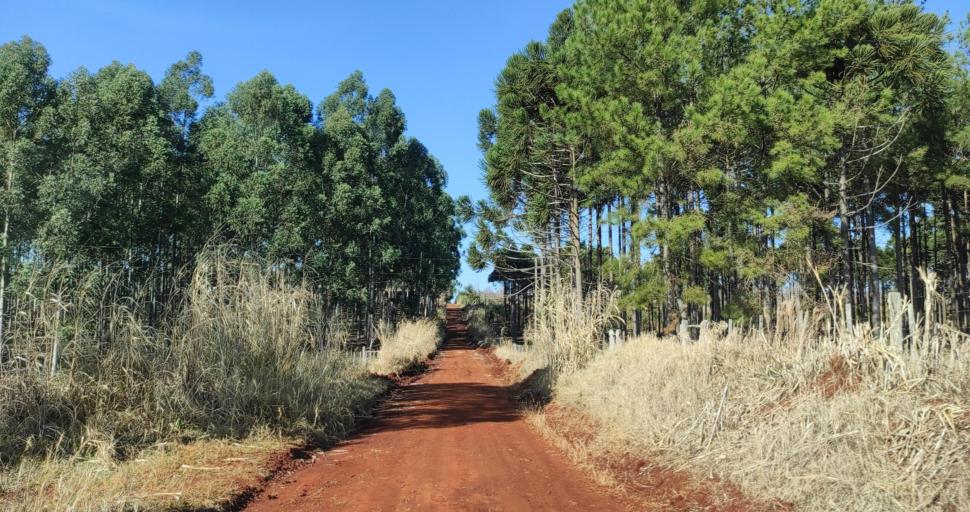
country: AR
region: Misiones
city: Capiovi
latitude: -26.8776
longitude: -55.0368
